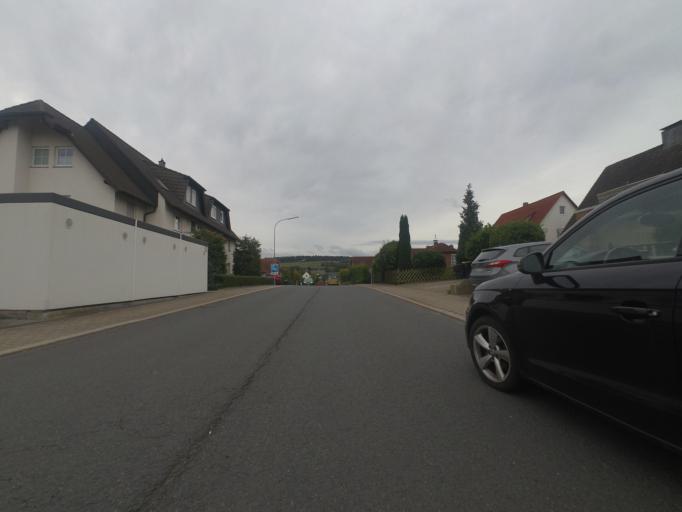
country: DE
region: North Rhine-Westphalia
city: Iserlohn
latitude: 51.4183
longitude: 7.6644
